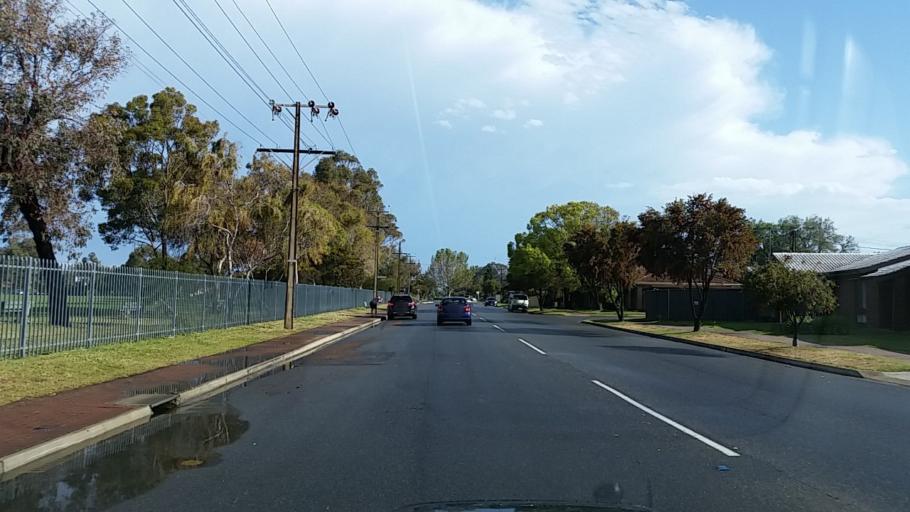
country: AU
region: South Australia
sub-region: Charles Sturt
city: Henley Beach
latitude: -34.9148
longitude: 138.5001
